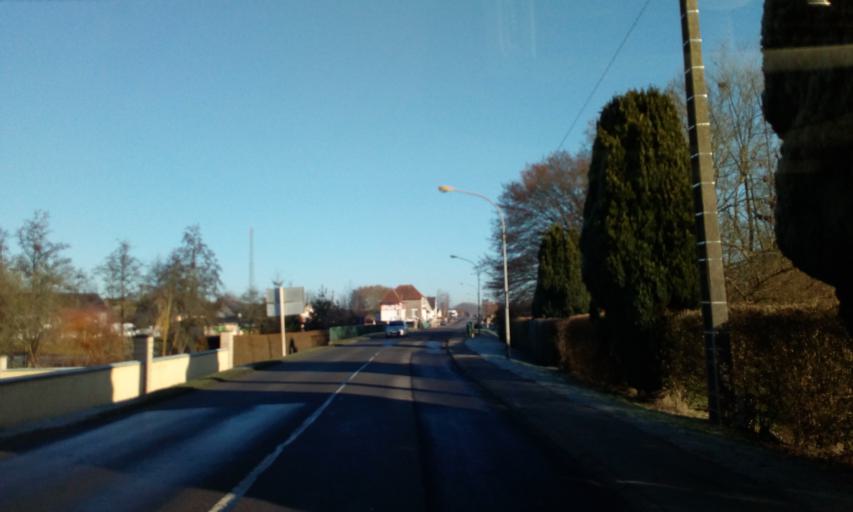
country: FR
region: Champagne-Ardenne
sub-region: Departement des Ardennes
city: Rimogne
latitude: 49.7897
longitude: 4.4969
